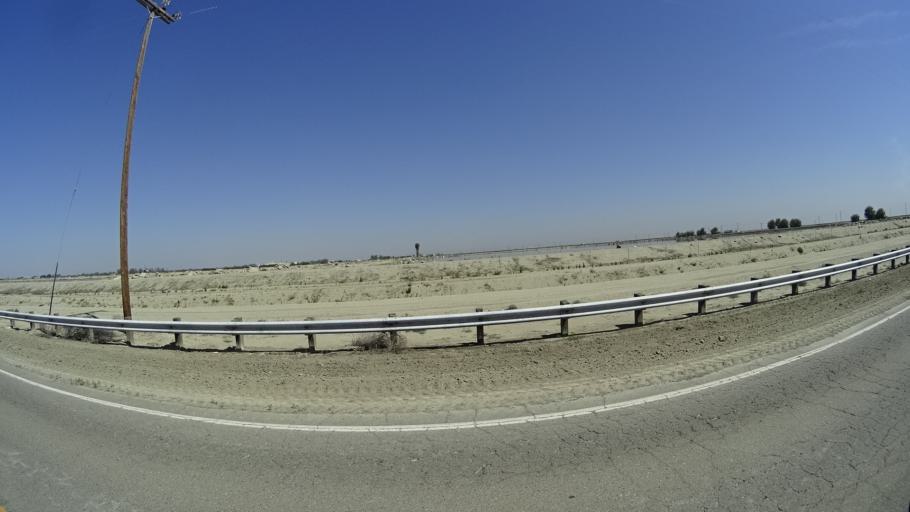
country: US
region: California
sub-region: Kings County
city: Corcoran
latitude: 36.0652
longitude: -119.5413
